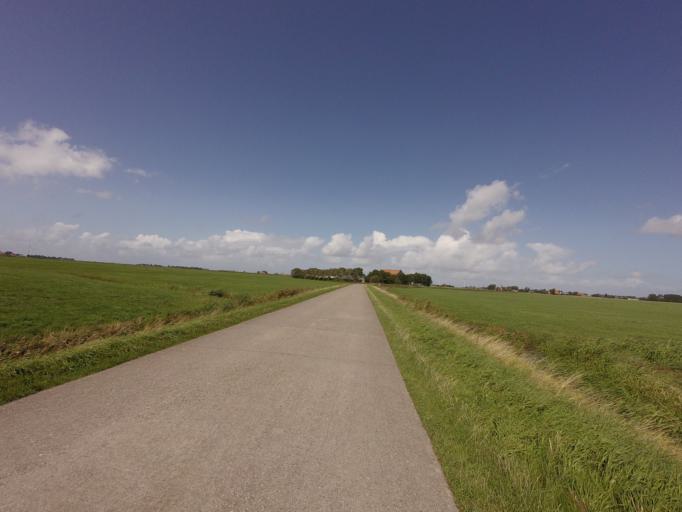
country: NL
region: Friesland
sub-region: Sudwest Fryslan
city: Makkum
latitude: 53.0684
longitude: 5.4560
